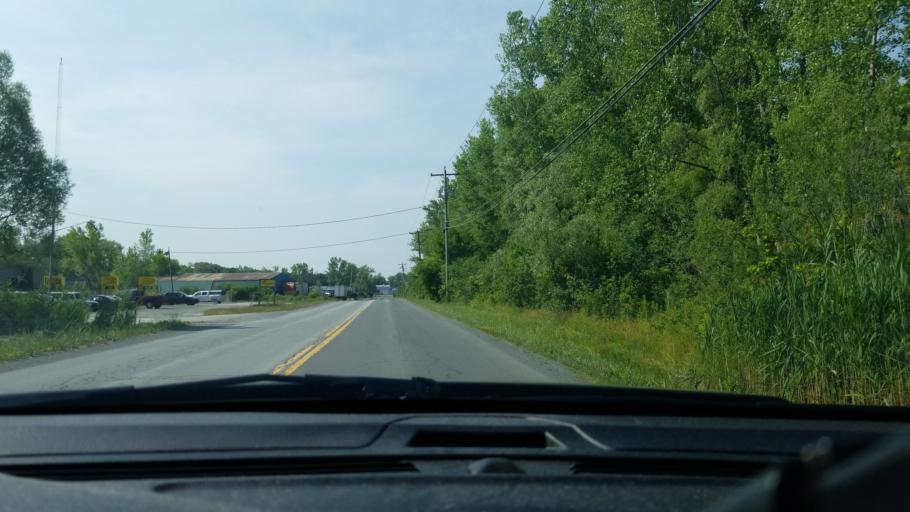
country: US
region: New York
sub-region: Onondaga County
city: North Syracuse
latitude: 43.1261
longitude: -76.0734
